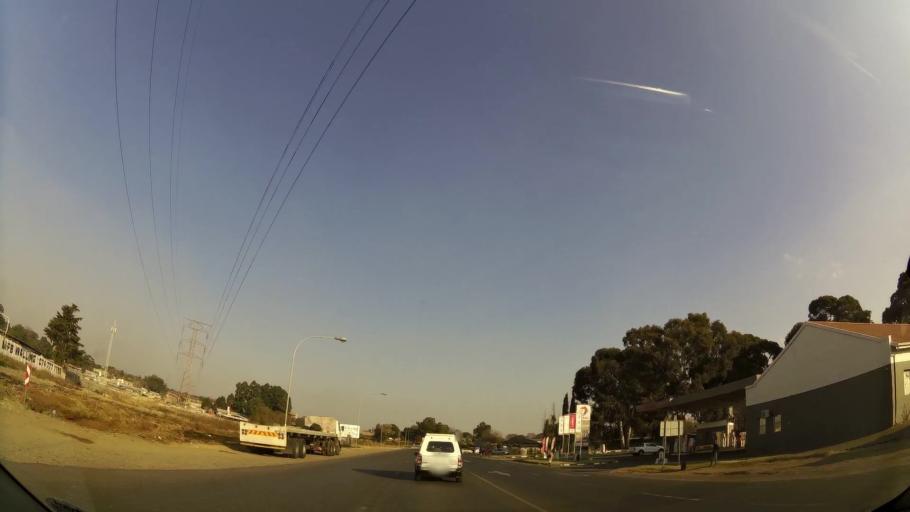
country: ZA
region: Gauteng
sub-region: Ekurhuleni Metropolitan Municipality
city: Benoni
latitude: -26.1336
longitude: 28.3898
